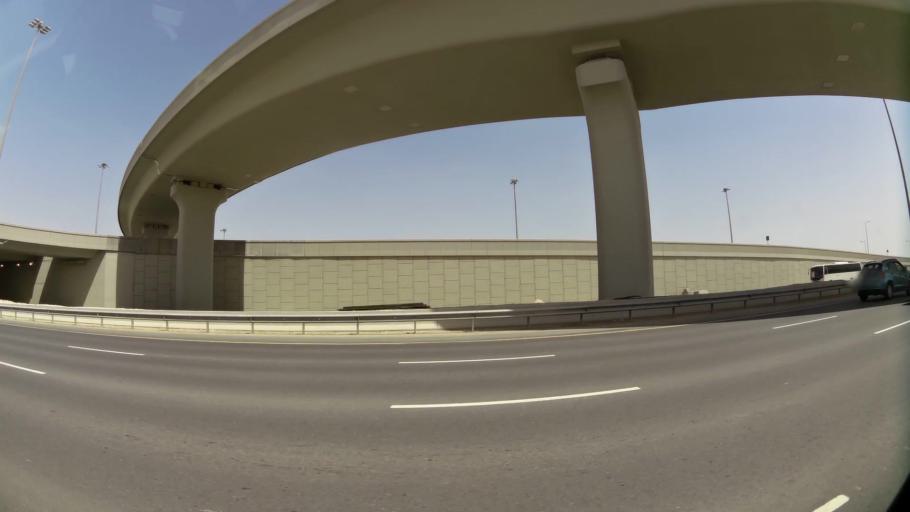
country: QA
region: Baladiyat Umm Salal
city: Umm Salal Muhammad
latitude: 25.3637
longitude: 51.4482
